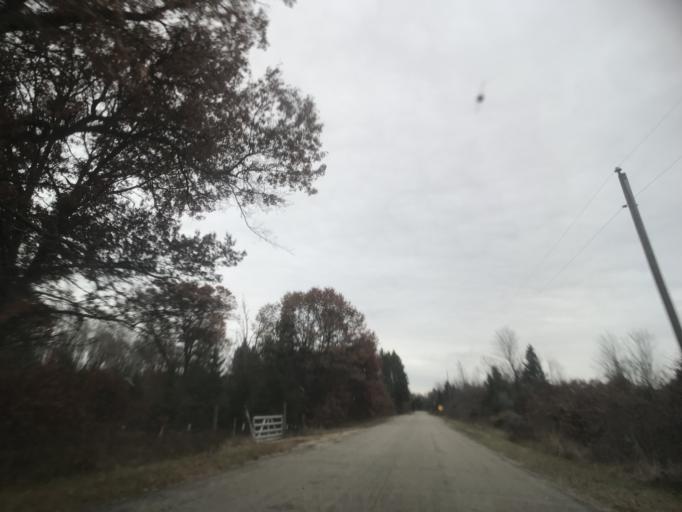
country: US
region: Wisconsin
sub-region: Oconto County
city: Gillett
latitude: 45.3162
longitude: -88.2766
